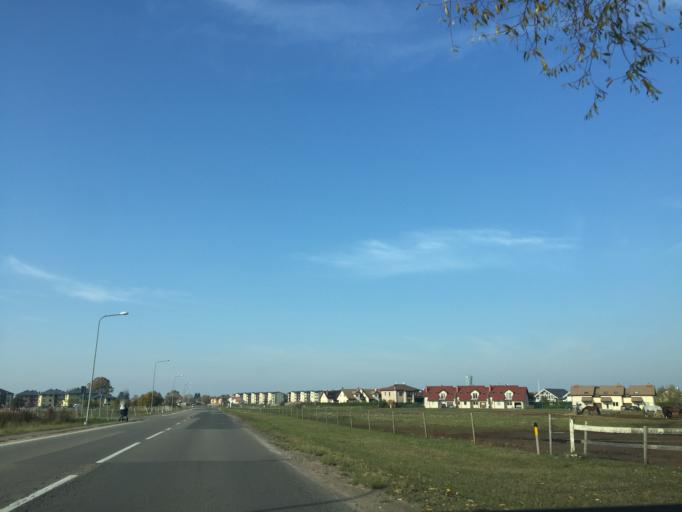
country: LV
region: Marupe
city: Marupe
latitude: 56.8886
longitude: 24.0612
